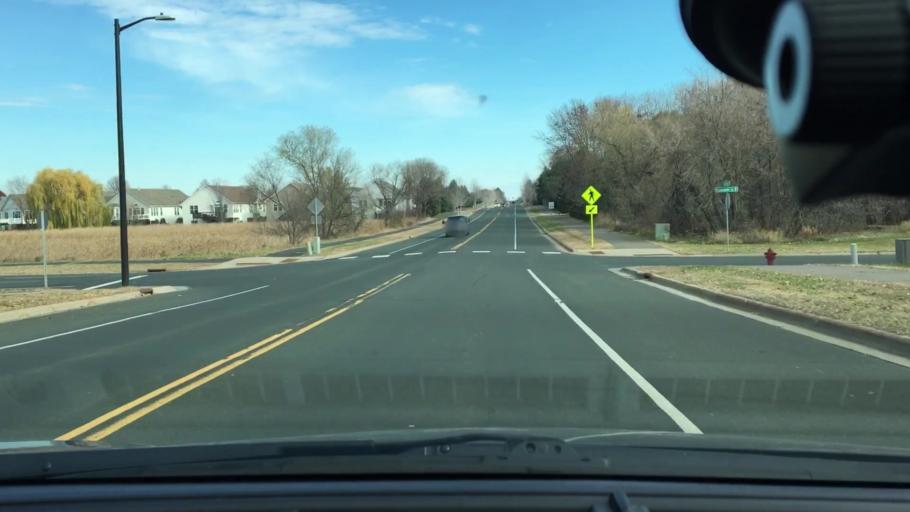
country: US
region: Minnesota
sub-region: Hennepin County
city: Corcoran
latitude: 45.1166
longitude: -93.5028
